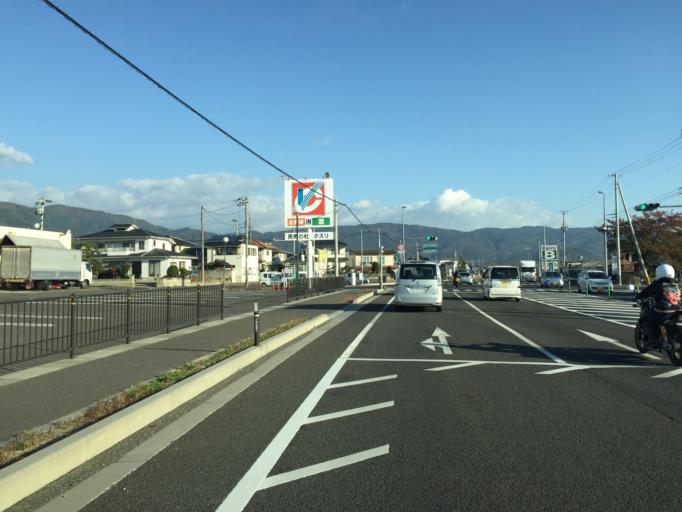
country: JP
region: Fukushima
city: Hobaramachi
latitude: 37.8561
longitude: 140.5226
